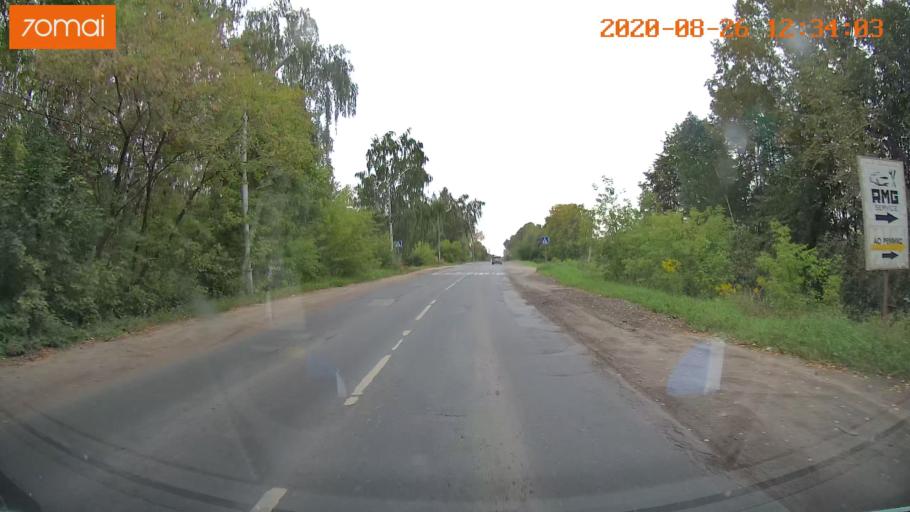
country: RU
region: Rjazan
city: Ryazan'
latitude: 54.5852
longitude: 39.7727
